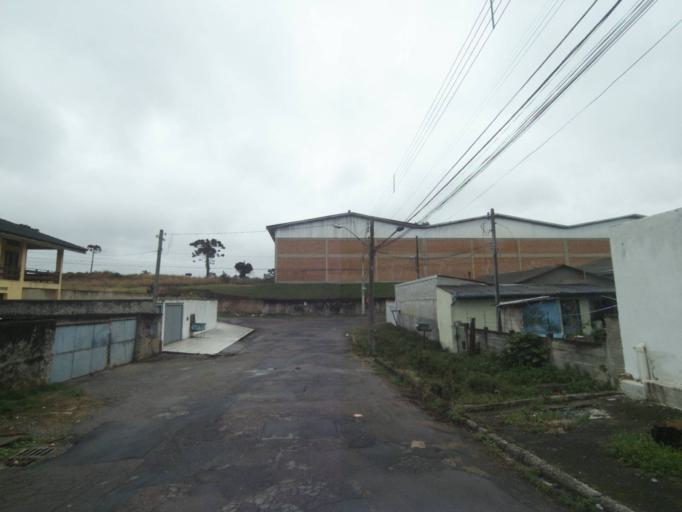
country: BR
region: Parana
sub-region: Curitiba
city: Curitiba
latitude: -25.5010
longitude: -49.3072
